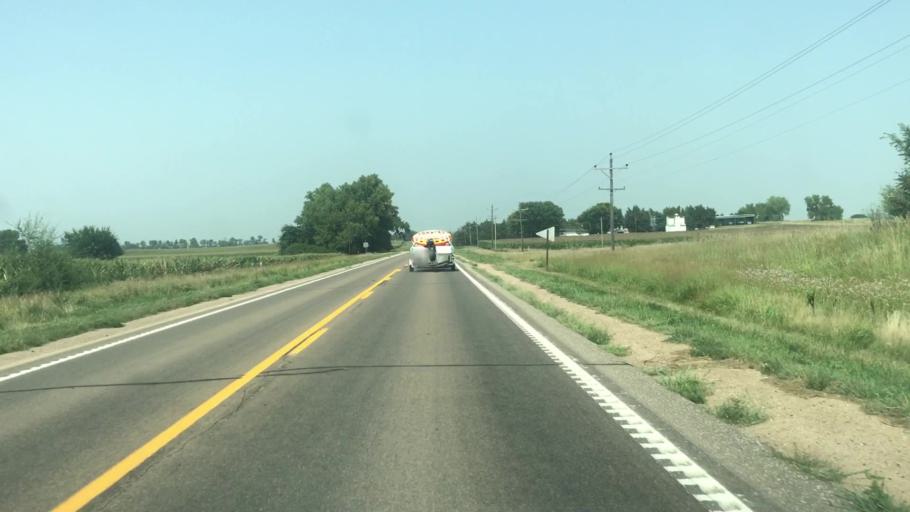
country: US
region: Nebraska
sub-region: Hall County
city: Wood River
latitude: 41.0166
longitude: -98.6074
